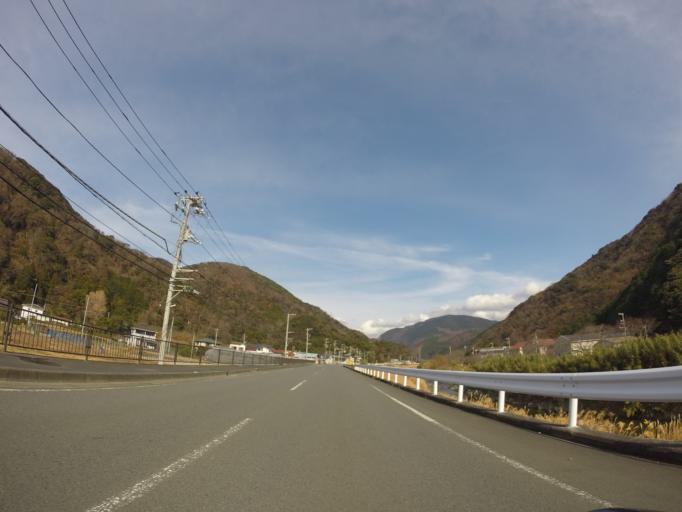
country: JP
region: Shizuoka
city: Heda
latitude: 34.7762
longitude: 138.7890
